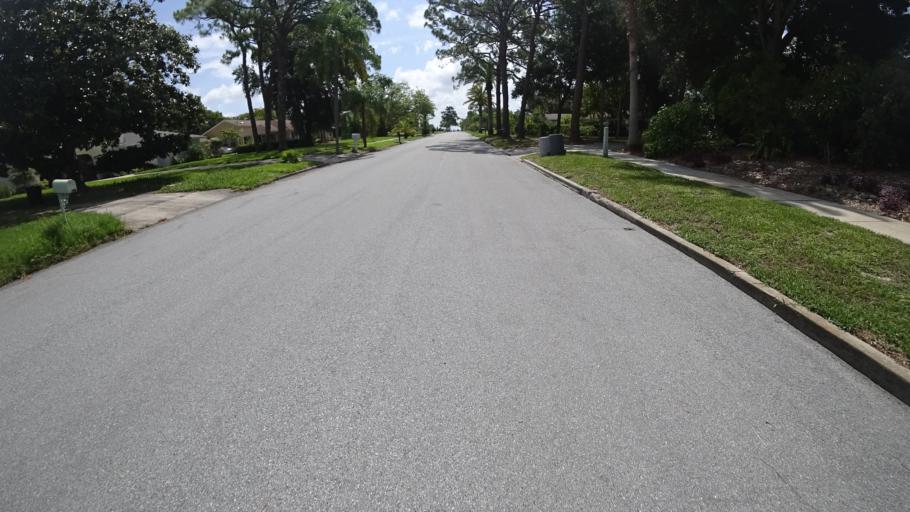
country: US
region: Florida
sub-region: Manatee County
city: Whitfield
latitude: 27.4001
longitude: -82.5687
